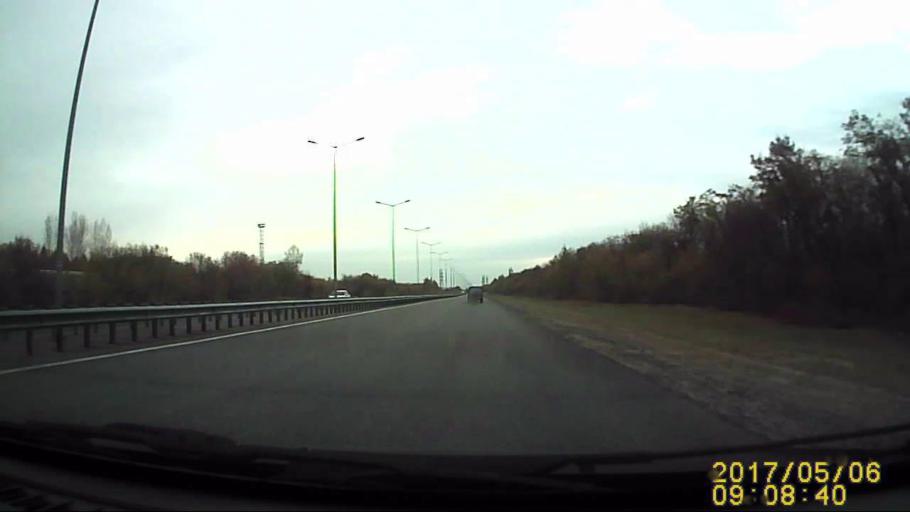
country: RU
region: Ulyanovsk
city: Mirnyy
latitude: 54.3426
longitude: 48.6248
